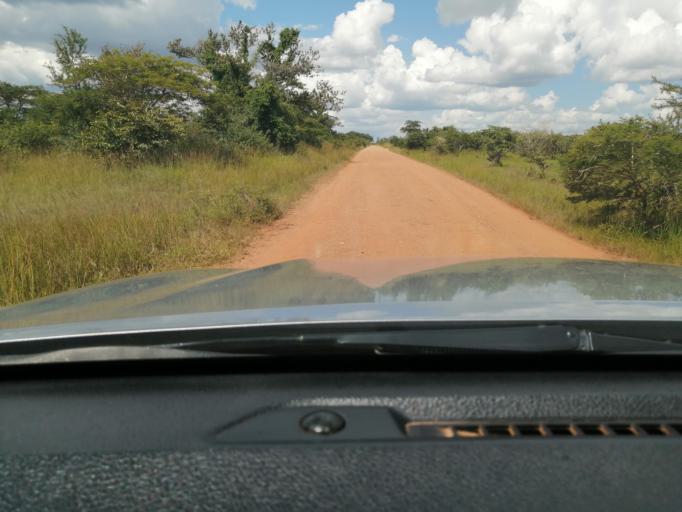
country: ZM
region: Lusaka
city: Lusaka
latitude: -15.1999
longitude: 28.0214
